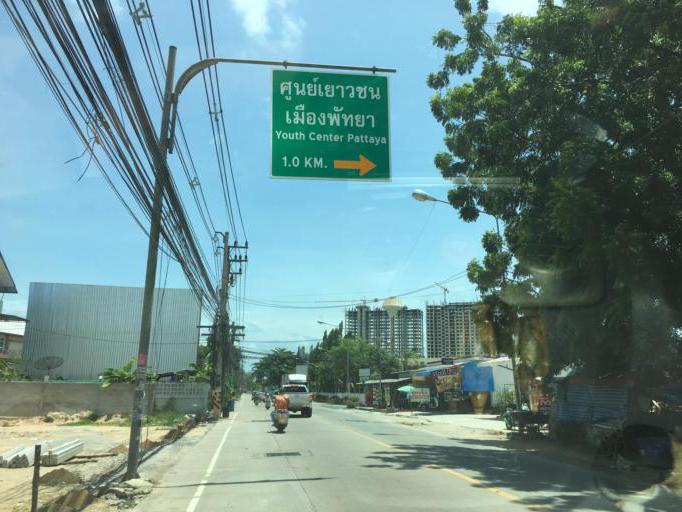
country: TH
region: Chon Buri
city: Phatthaya
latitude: 12.8899
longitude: 100.8940
